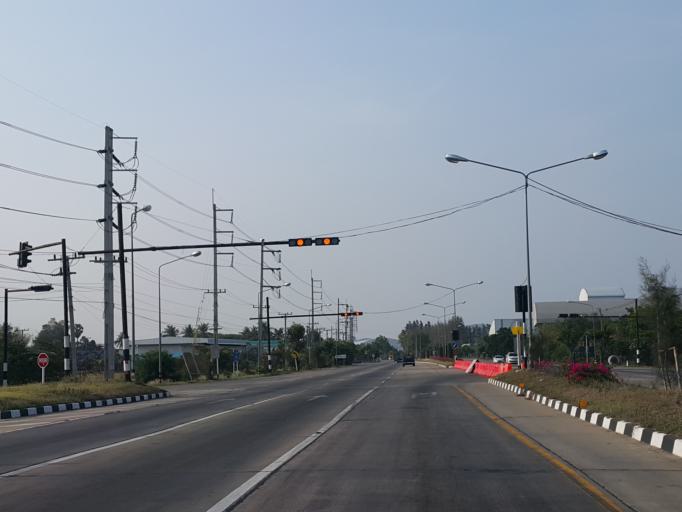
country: TH
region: Chai Nat
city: Hankha
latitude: 14.9430
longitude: 100.0815
